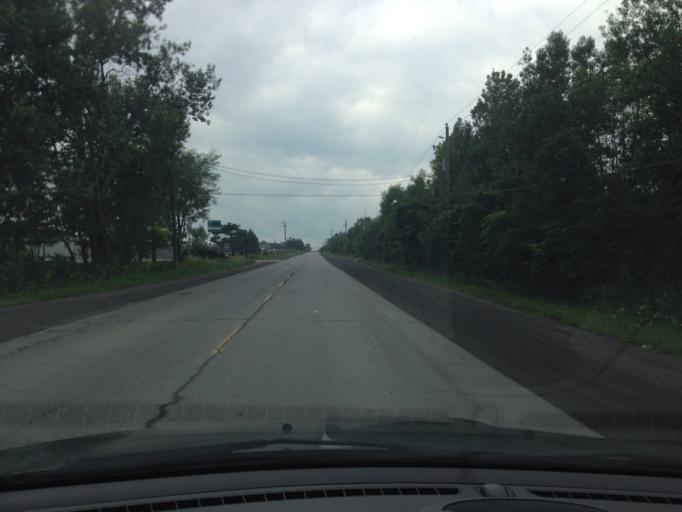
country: CA
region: Ontario
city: Ottawa
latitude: 45.3010
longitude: -75.5698
